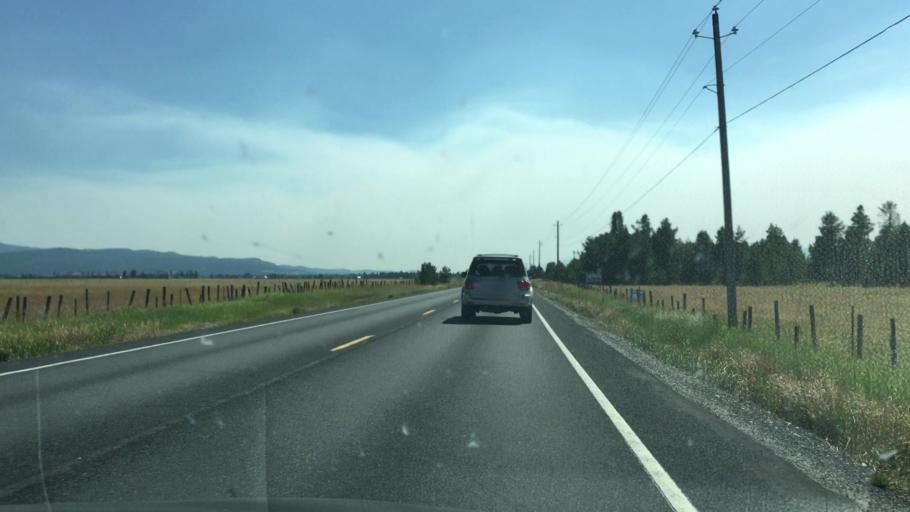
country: US
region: Idaho
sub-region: Valley County
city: McCall
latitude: 44.7583
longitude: -116.0783
